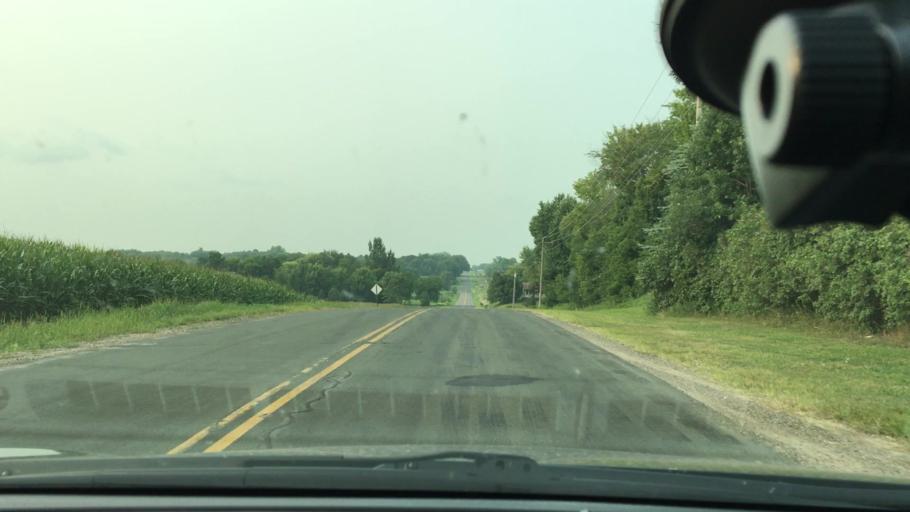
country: US
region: Minnesota
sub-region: Wright County
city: Albertville
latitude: 45.2746
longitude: -93.6841
